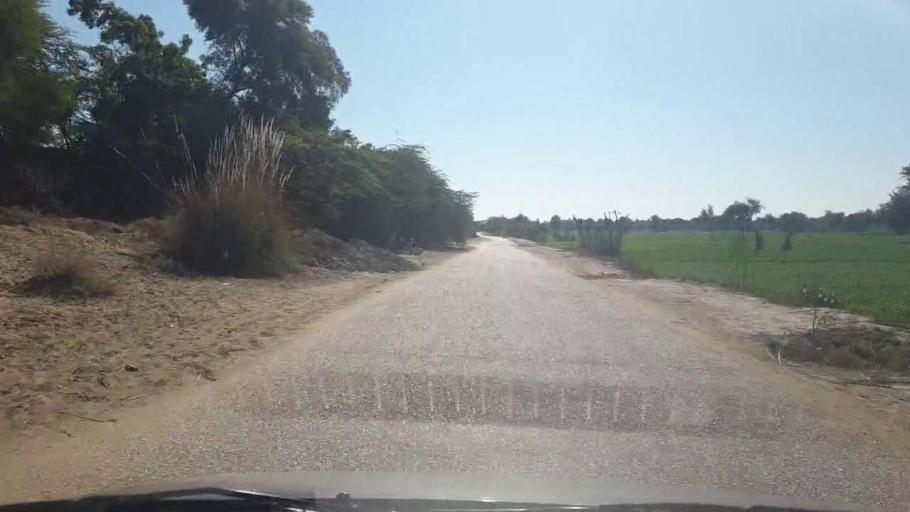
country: PK
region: Sindh
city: Bozdar
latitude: 27.0550
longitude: 68.6479
